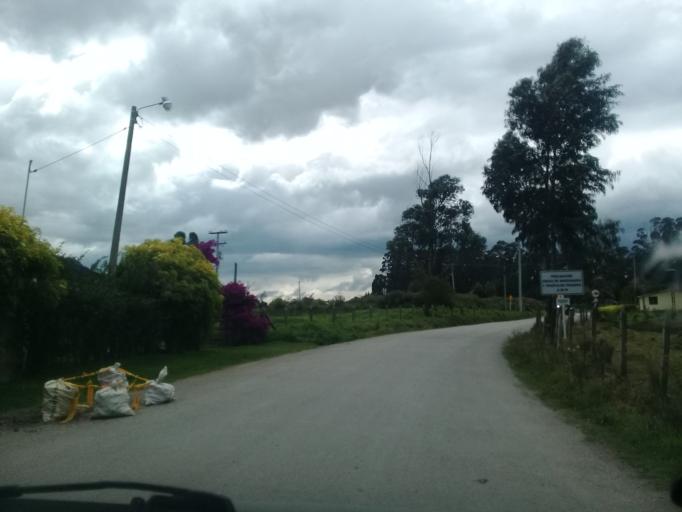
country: CO
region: Cundinamarca
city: Tenjo
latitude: 4.8578
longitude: -74.1982
